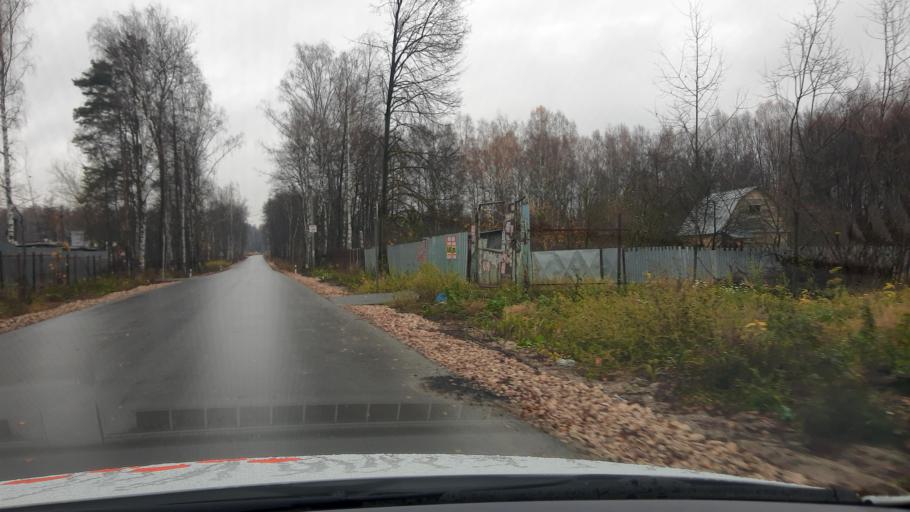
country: RU
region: Moskovskaya
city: Elektrostal'
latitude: 55.7946
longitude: 38.3697
